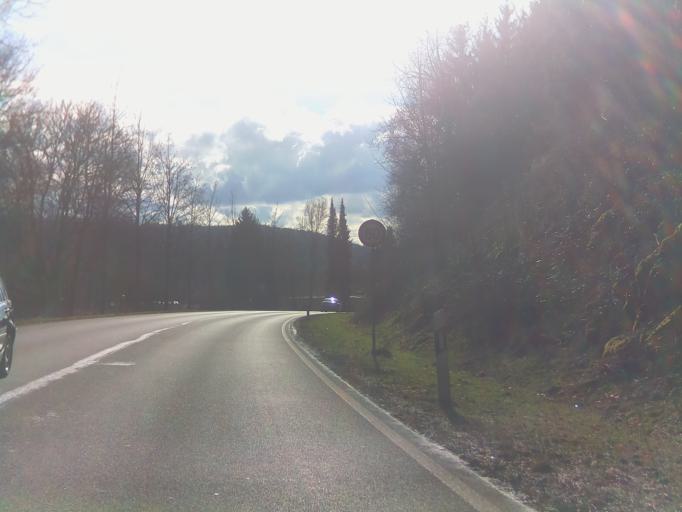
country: DE
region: Hesse
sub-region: Regierungsbezirk Darmstadt
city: Hirzenhain
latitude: 50.3950
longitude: 9.1385
